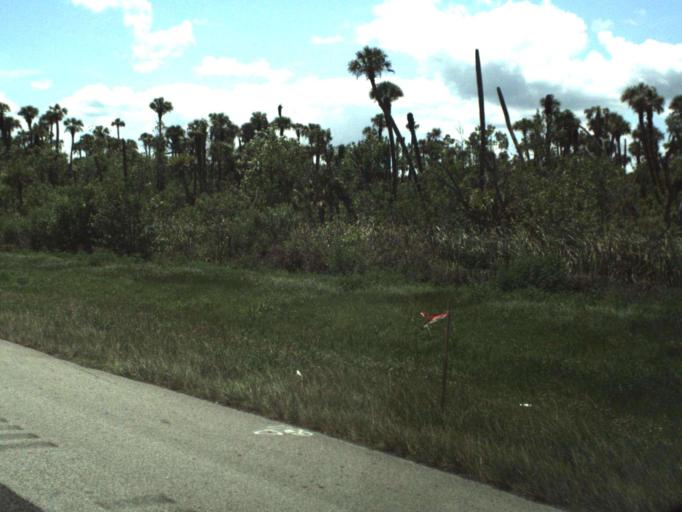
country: US
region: Florida
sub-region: Volusia County
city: DeBary
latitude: 28.8443
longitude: -81.3107
